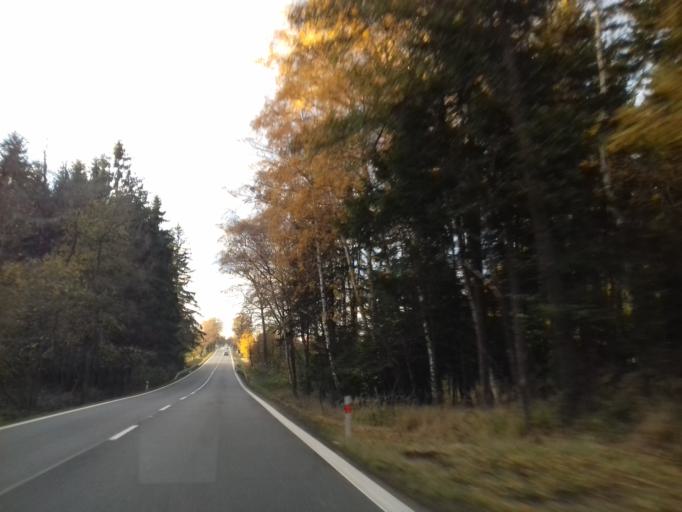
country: CZ
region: Pardubicky
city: Krouna
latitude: 49.7689
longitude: 16.0552
